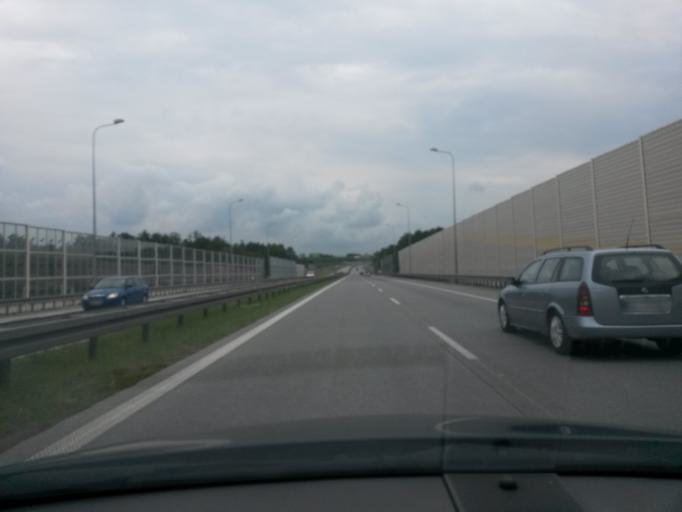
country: PL
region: Lodz Voivodeship
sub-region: Powiat skierniewicki
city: Kowiesy
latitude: 51.8903
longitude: 20.4205
